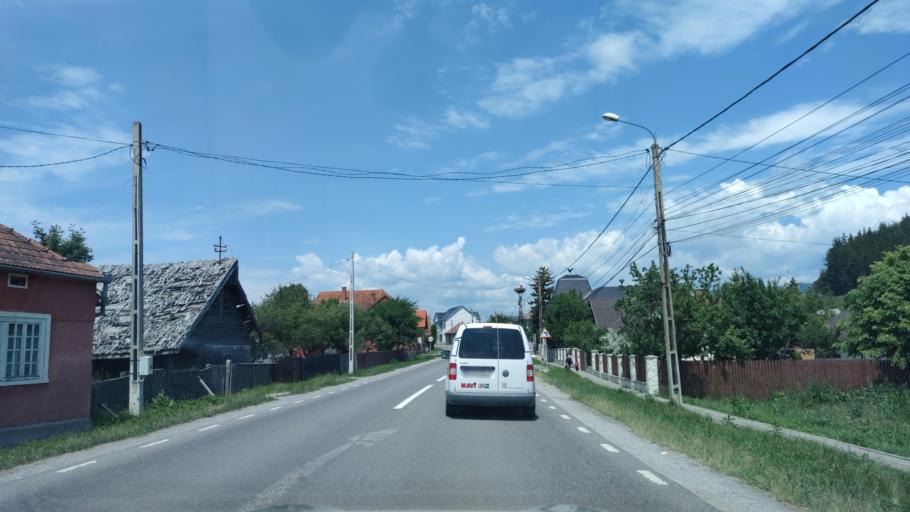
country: RO
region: Harghita
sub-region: Comuna Voslobeni
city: Voslobeni
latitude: 46.6413
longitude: 25.6243
